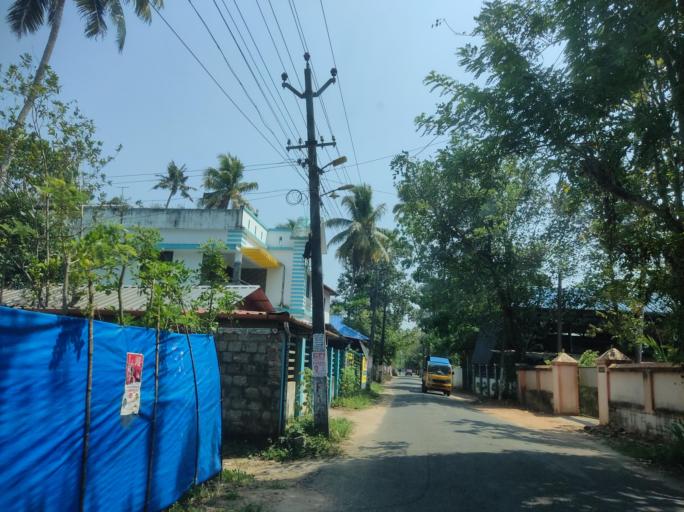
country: IN
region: Kerala
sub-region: Alappuzha
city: Vayalar
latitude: 9.6962
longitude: 76.3028
